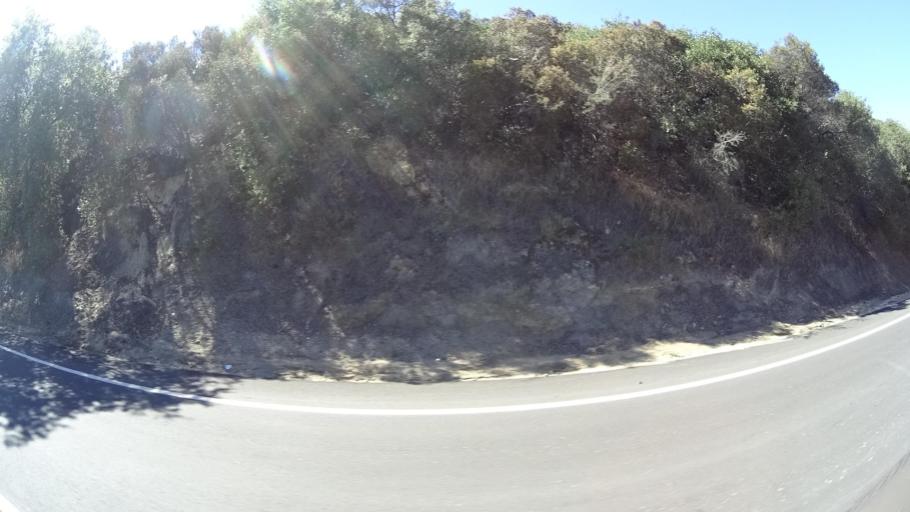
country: US
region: California
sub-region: San Diego County
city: Jamul
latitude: 32.7298
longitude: -116.7849
